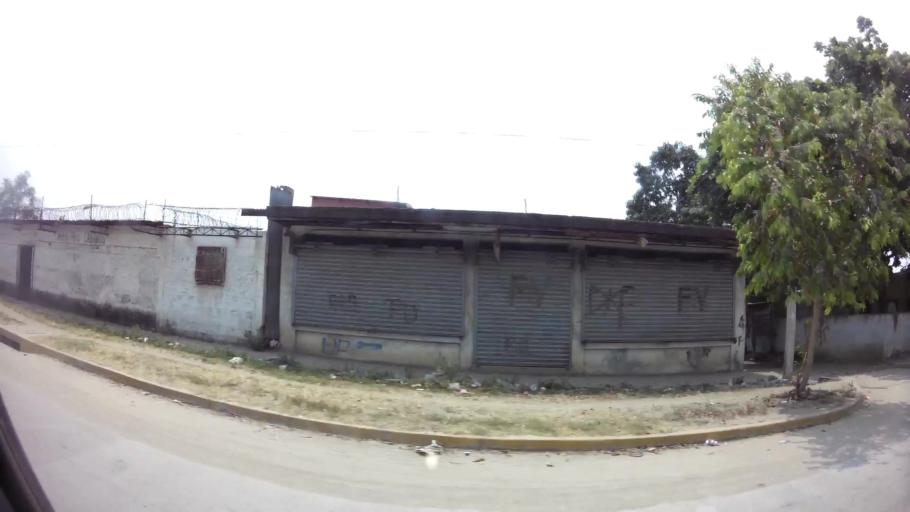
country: HN
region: Cortes
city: San Pedro Sula
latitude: 15.4779
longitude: -88.0222
